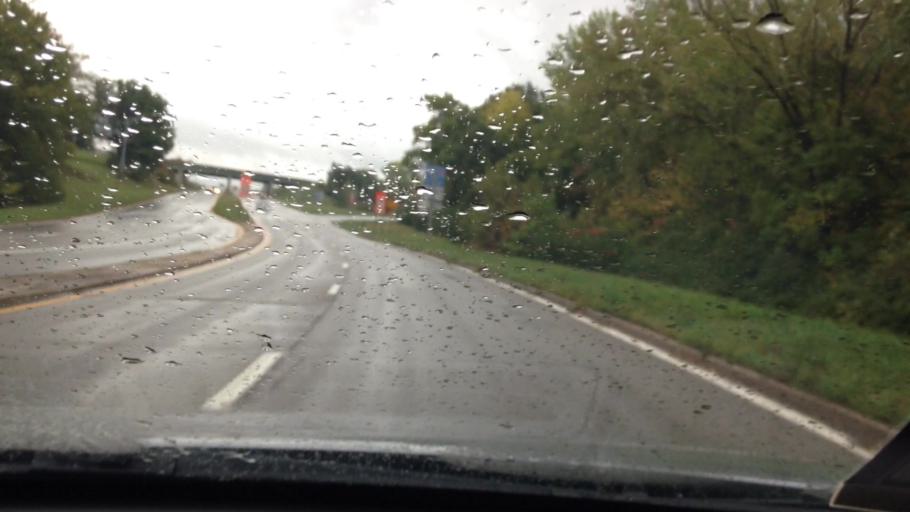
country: US
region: Missouri
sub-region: Platte County
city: Riverside
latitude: 39.1798
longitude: -94.5896
